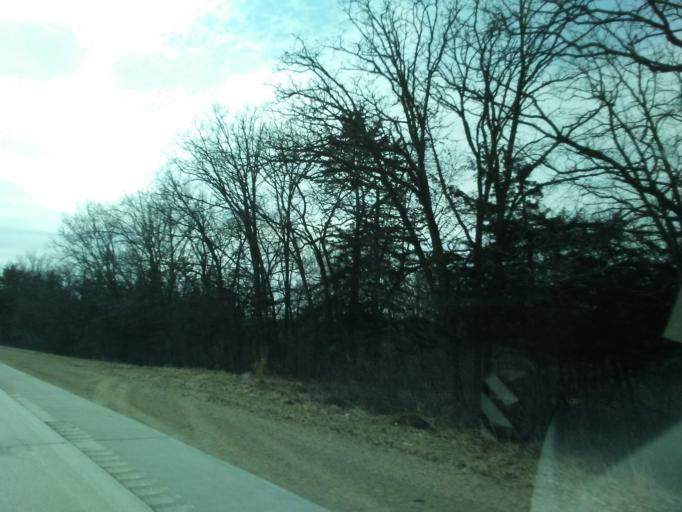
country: US
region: Iowa
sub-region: Winneshiek County
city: Decorah
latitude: 43.3416
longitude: -91.8106
